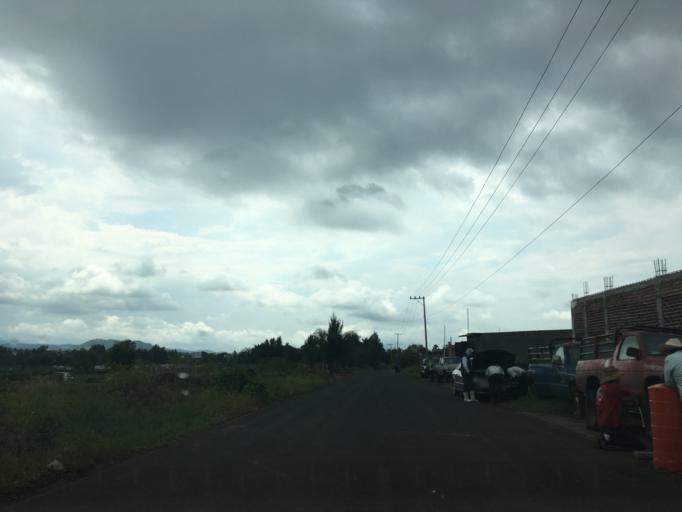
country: MX
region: Michoacan
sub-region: Periban
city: Gildardo Magana (Los Angeles)
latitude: 19.5780
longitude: -102.4541
